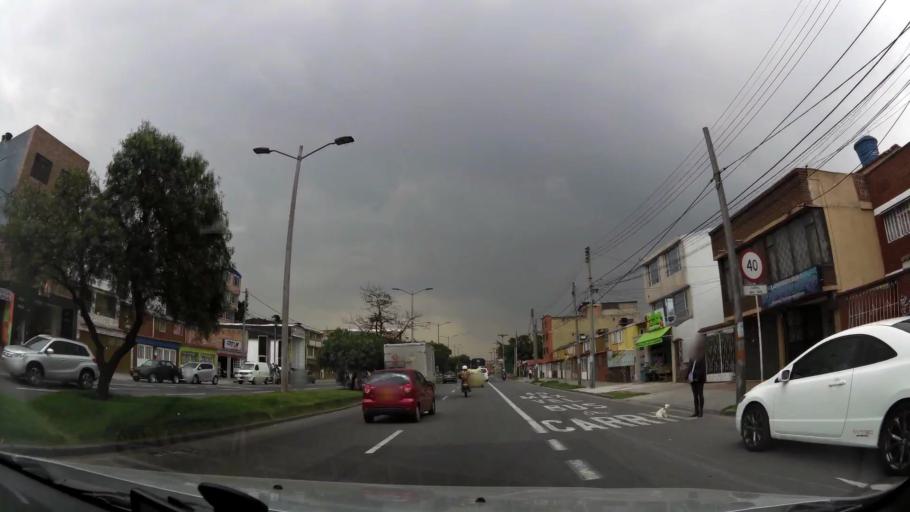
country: CO
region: Bogota D.C.
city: Bogota
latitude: 4.6089
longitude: -74.1177
